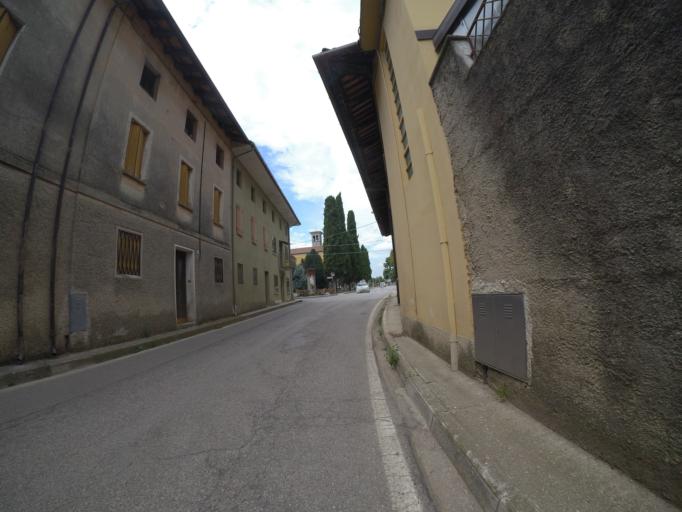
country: IT
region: Friuli Venezia Giulia
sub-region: Provincia di Udine
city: Castions di Strada
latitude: 45.9174
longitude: 13.1563
